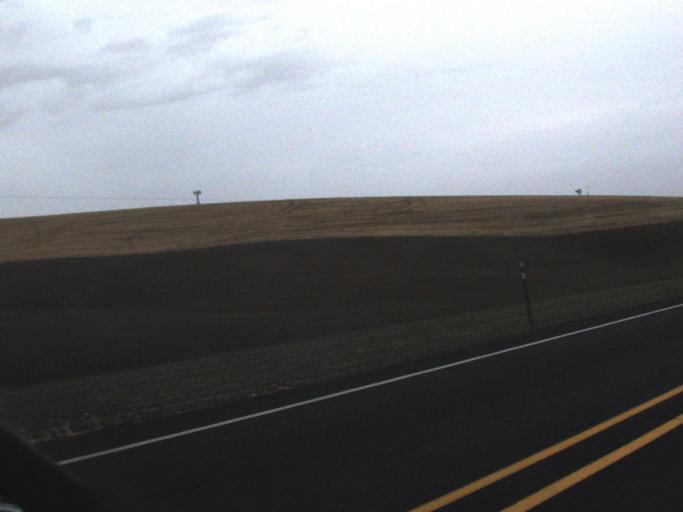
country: US
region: Washington
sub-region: Whitman County
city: Colfax
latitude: 46.8125
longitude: -117.6603
